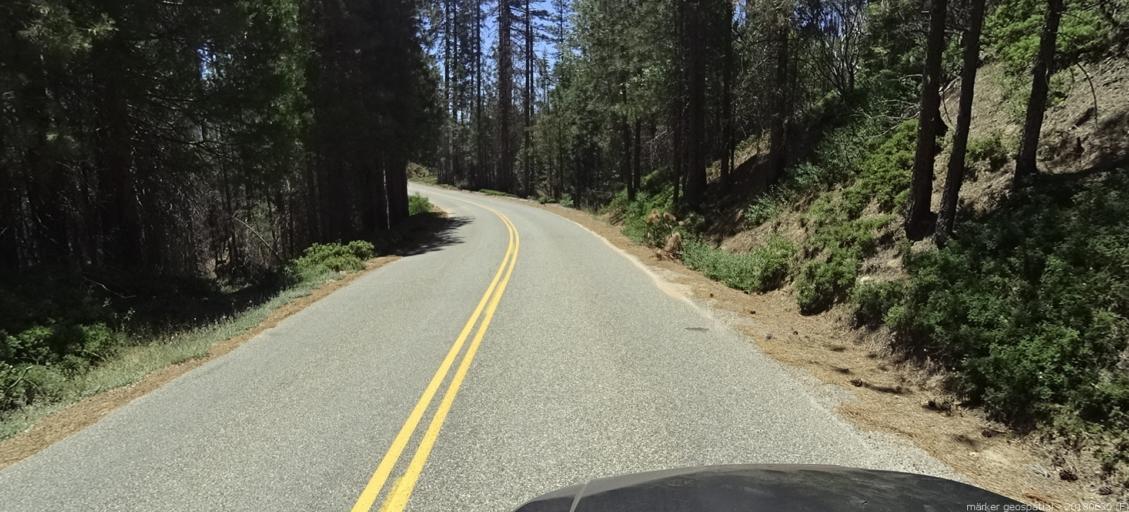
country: US
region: California
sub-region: Fresno County
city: Auberry
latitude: 37.3326
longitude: -119.3689
